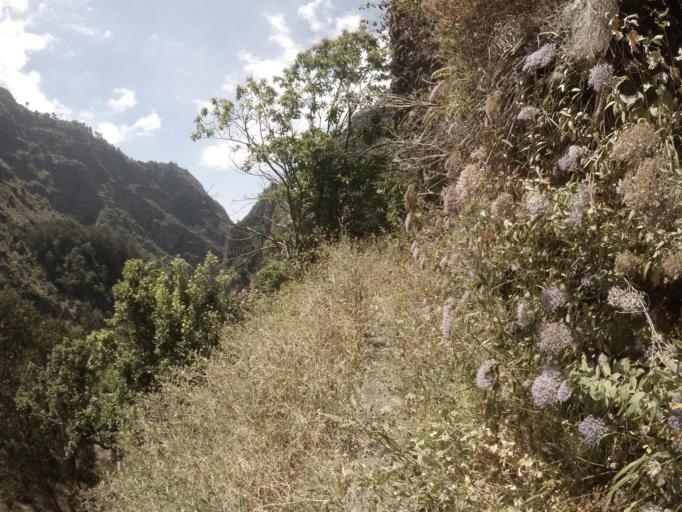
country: PT
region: Madeira
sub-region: Camara de Lobos
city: Curral das Freiras
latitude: 32.7029
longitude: -16.9659
